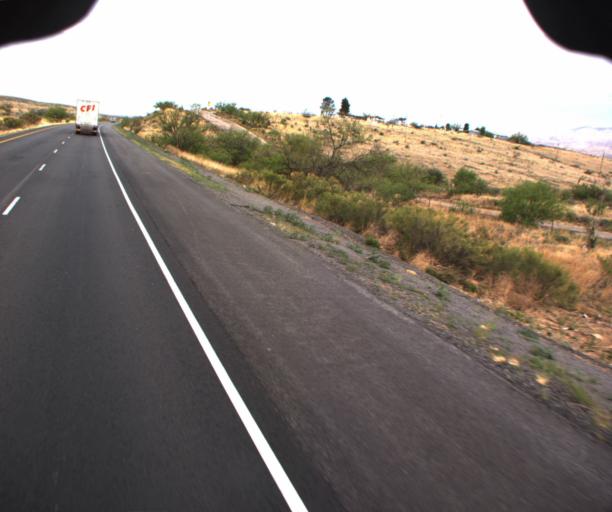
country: US
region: Arizona
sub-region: Cochise County
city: Mescal
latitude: 31.9644
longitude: -110.4560
